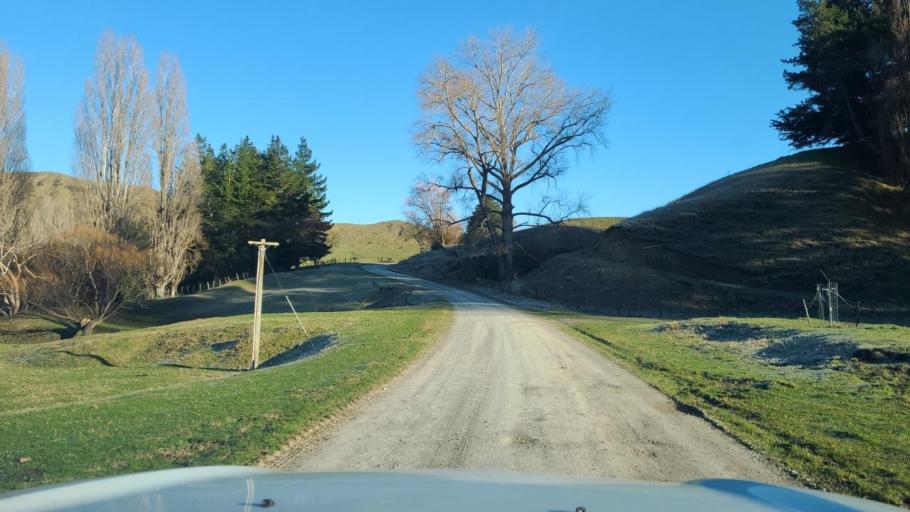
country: NZ
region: Hawke's Bay
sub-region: Hastings District
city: Hastings
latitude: -39.7989
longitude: 176.8334
